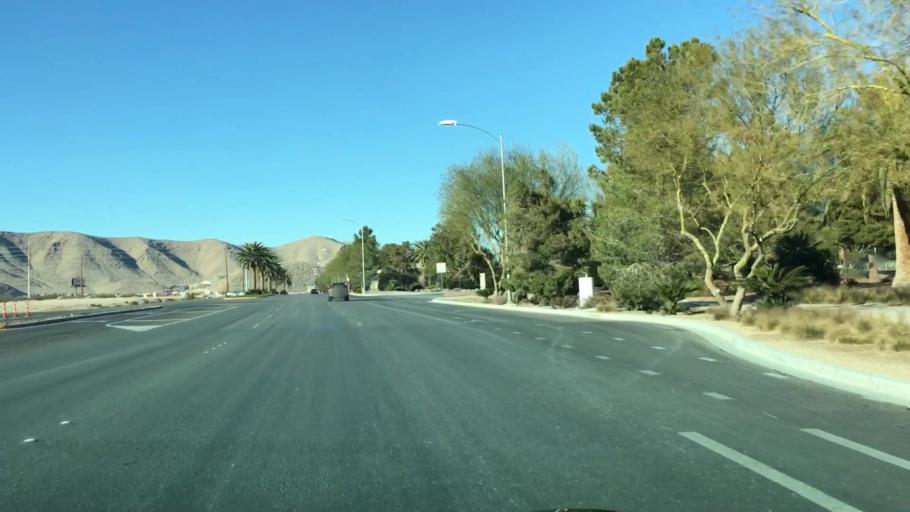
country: US
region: Nevada
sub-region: Clark County
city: Enterprise
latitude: 35.9637
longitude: -115.1686
